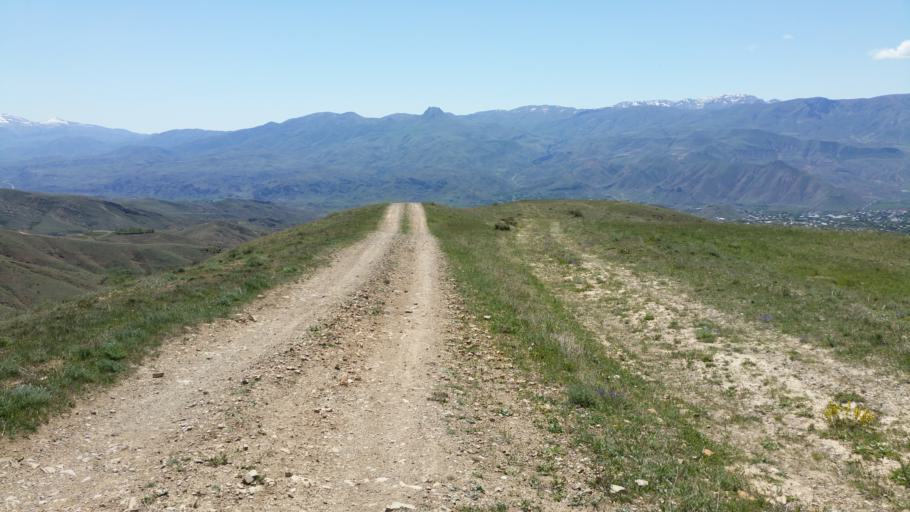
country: AM
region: Vayots' Dzori Marz
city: Vernashen
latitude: 39.8022
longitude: 45.3605
